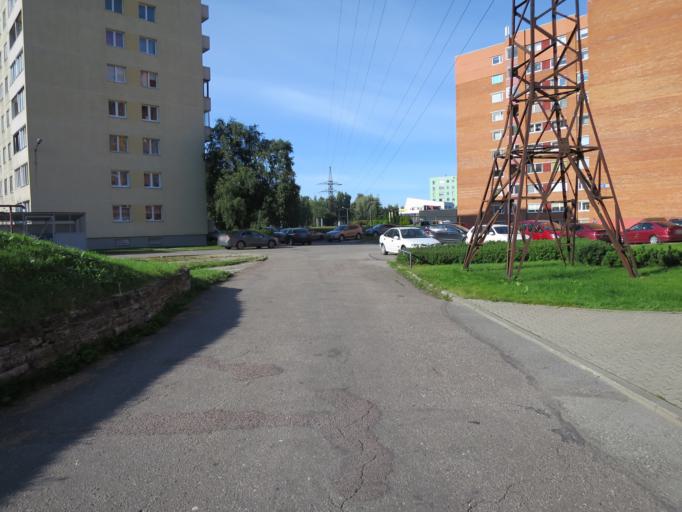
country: EE
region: Harju
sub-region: Tallinna linn
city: Tallinn
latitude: 59.4087
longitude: 24.7065
